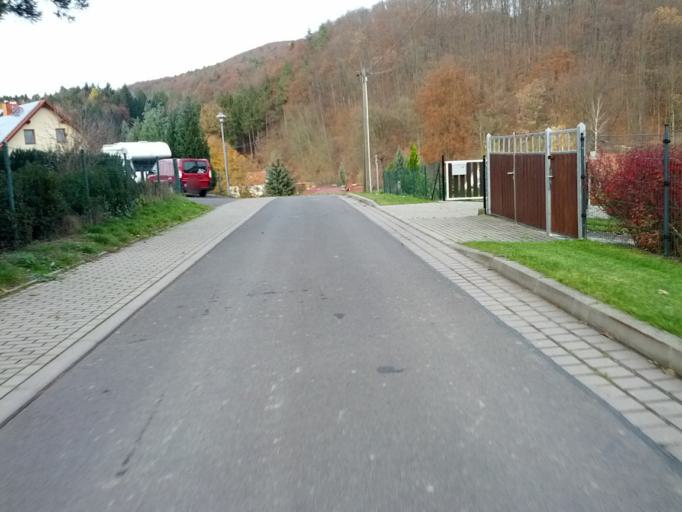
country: DE
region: Thuringia
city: Ruhla
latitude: 50.9352
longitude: 10.3513
